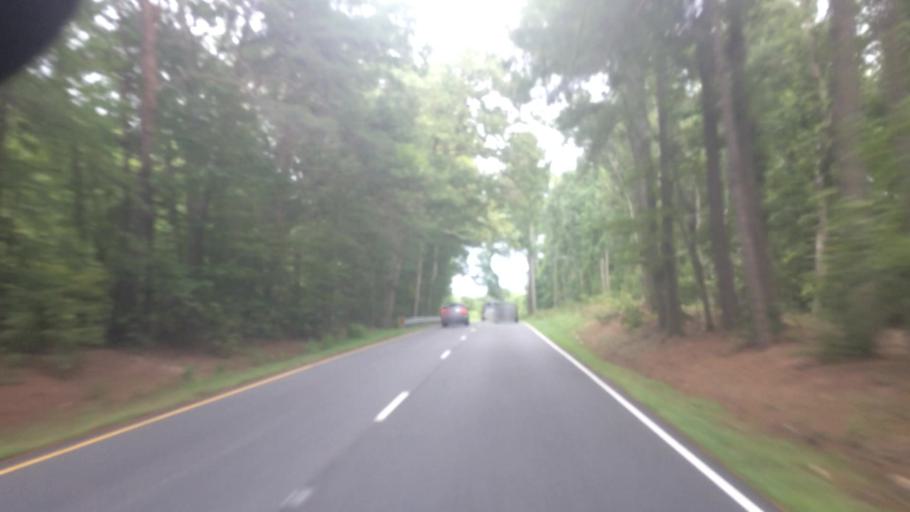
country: US
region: Virginia
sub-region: King William County
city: West Point
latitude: 37.4121
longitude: -76.8154
